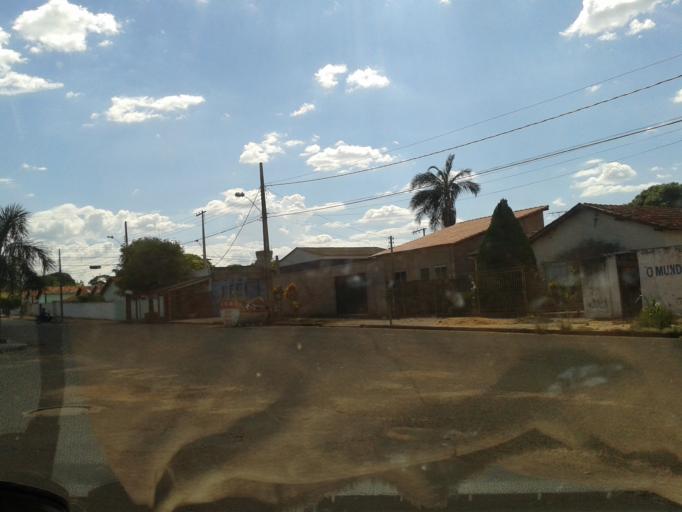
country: BR
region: Minas Gerais
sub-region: Ituiutaba
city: Ituiutaba
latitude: -18.9851
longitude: -49.4513
